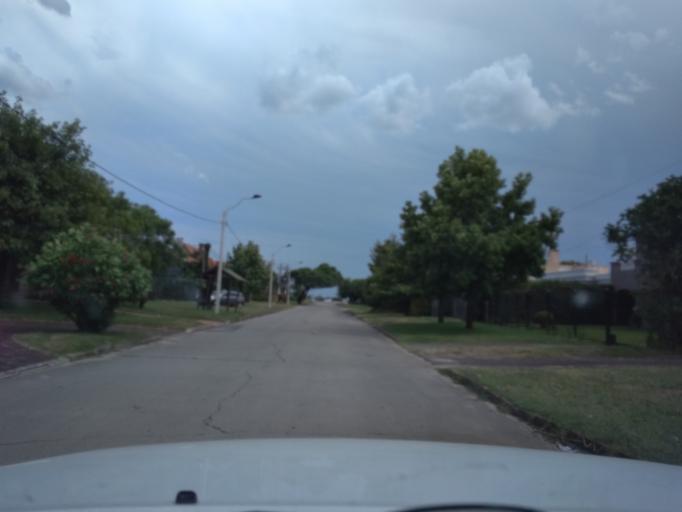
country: UY
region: Canelones
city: Barra de Carrasco
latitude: -34.8855
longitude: -56.0479
